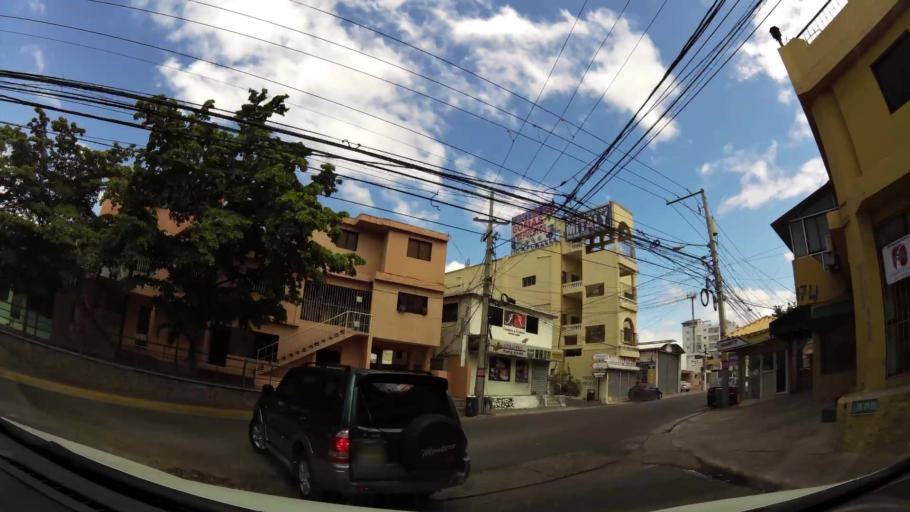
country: DO
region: Nacional
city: Bella Vista
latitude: 18.4685
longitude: -69.9479
